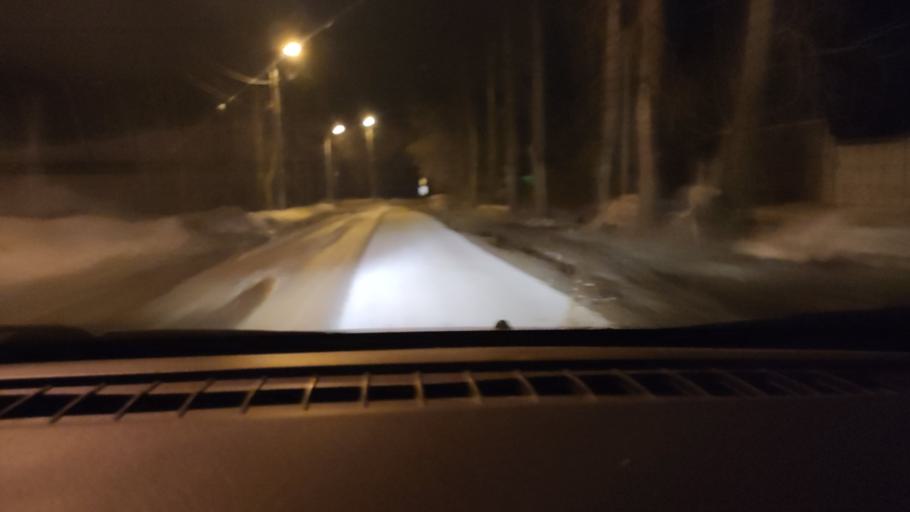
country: RU
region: Perm
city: Perm
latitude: 58.0976
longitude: 56.3682
